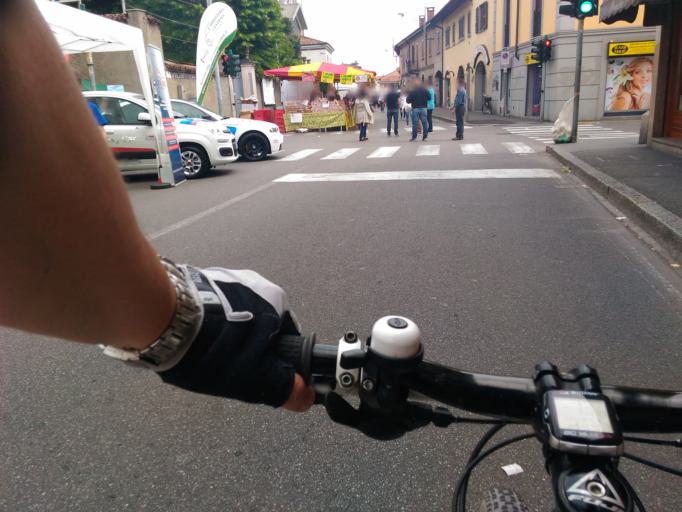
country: IT
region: Lombardy
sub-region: Citta metropolitana di Milano
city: Paullo
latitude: 45.4160
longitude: 9.4004
